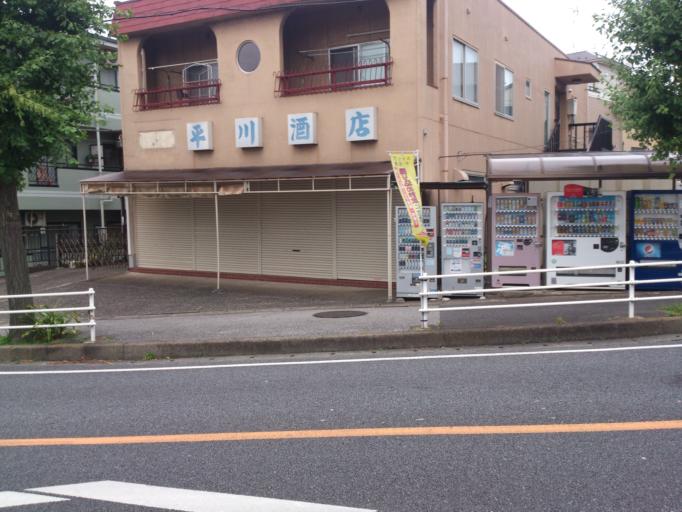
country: JP
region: Chiba
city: Matsudo
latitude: 35.7903
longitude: 139.9156
